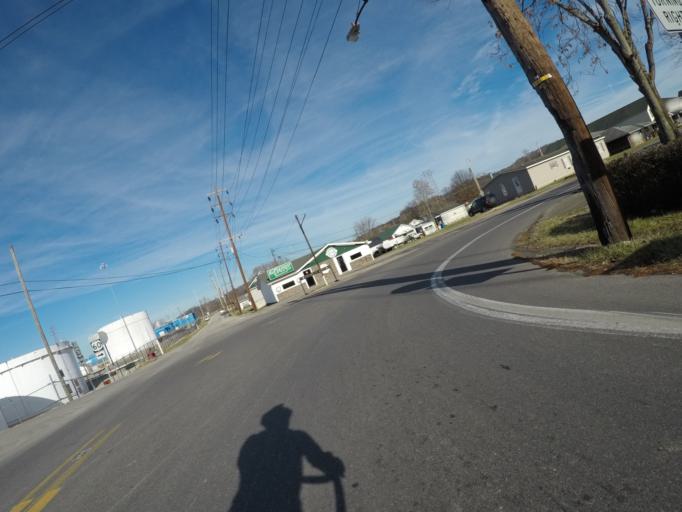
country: US
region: West Virginia
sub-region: Wayne County
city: Kenova
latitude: 38.4039
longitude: -82.5873
